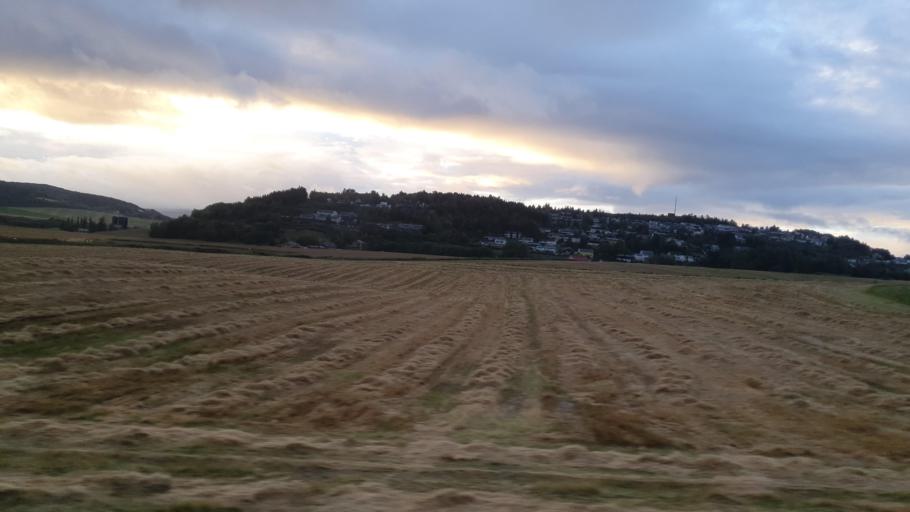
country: NO
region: Nord-Trondelag
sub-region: Levanger
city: Skogn
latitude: 63.6927
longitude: 11.1928
